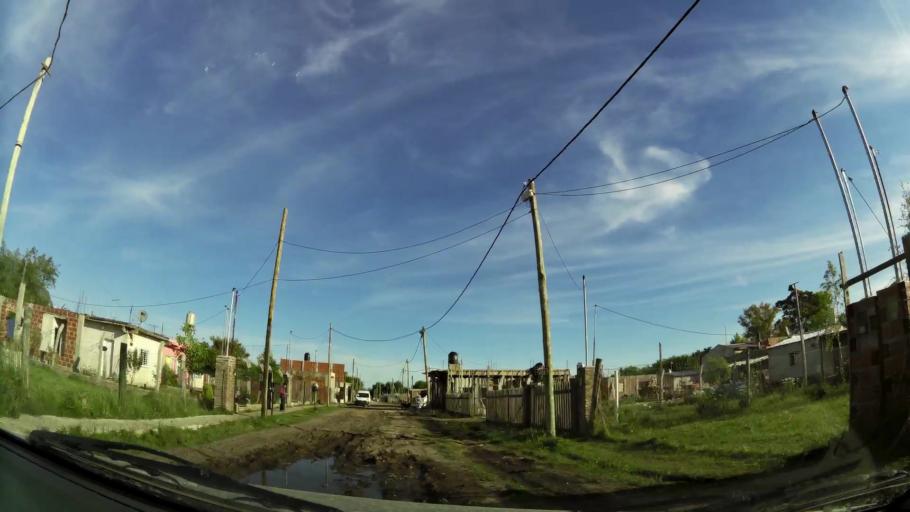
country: AR
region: Buenos Aires
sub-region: Partido de Almirante Brown
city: Adrogue
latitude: -34.8196
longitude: -58.3259
